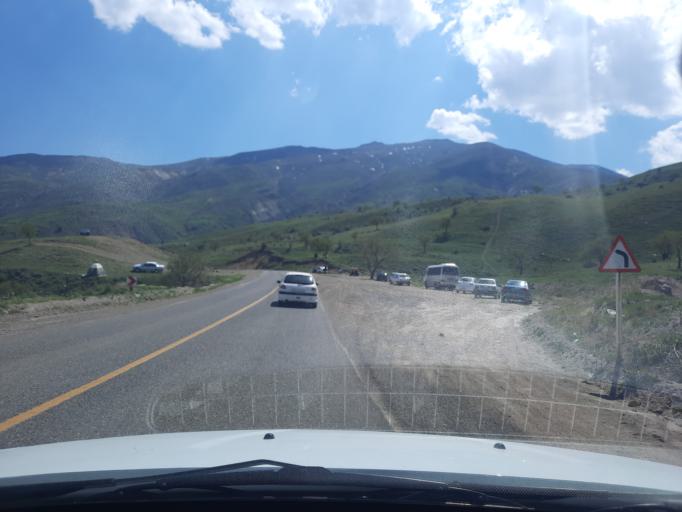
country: IR
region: Qazvin
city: Qazvin
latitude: 36.4108
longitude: 50.2442
